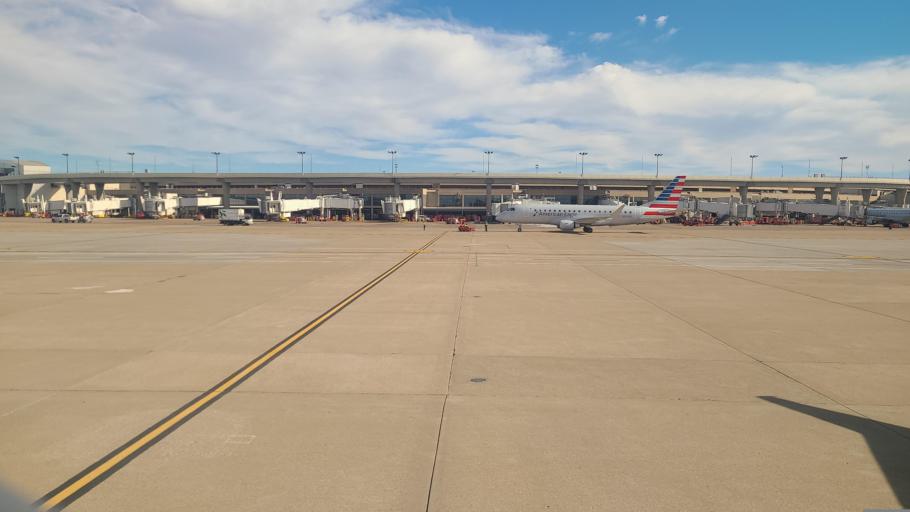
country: US
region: Texas
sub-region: Tarrant County
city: Grapevine
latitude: 32.9047
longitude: -97.0476
